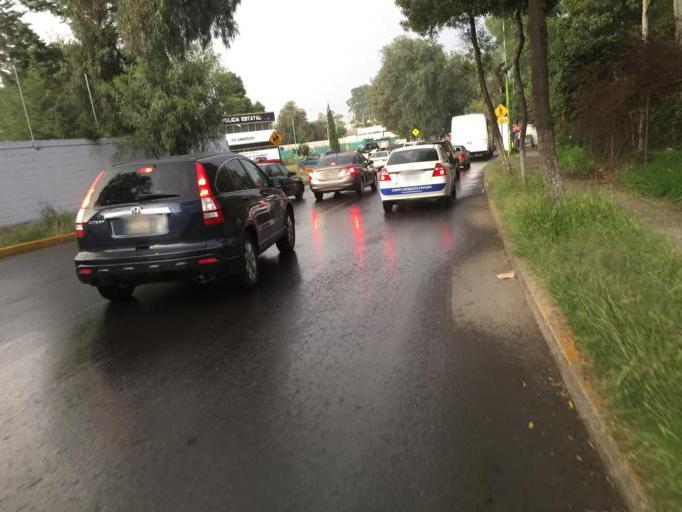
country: MX
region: Mexico
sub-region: Cuautitlan Izcalli
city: Axotlan
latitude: 19.6762
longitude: -99.2139
